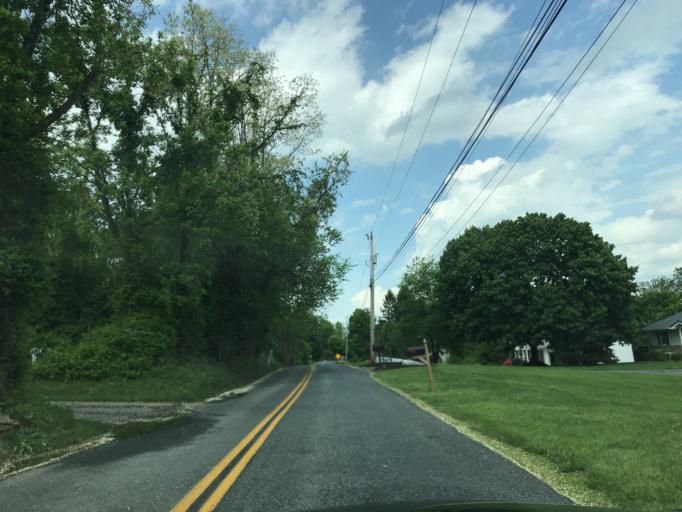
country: US
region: Pennsylvania
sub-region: York County
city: Susquehanna Trails
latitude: 39.7027
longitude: -76.3323
